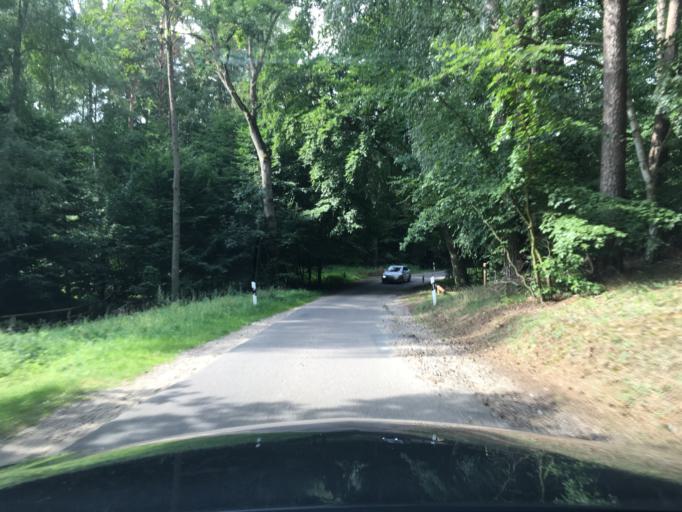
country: DE
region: Mecklenburg-Vorpommern
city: Mollenhagen
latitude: 53.4504
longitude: 12.8207
